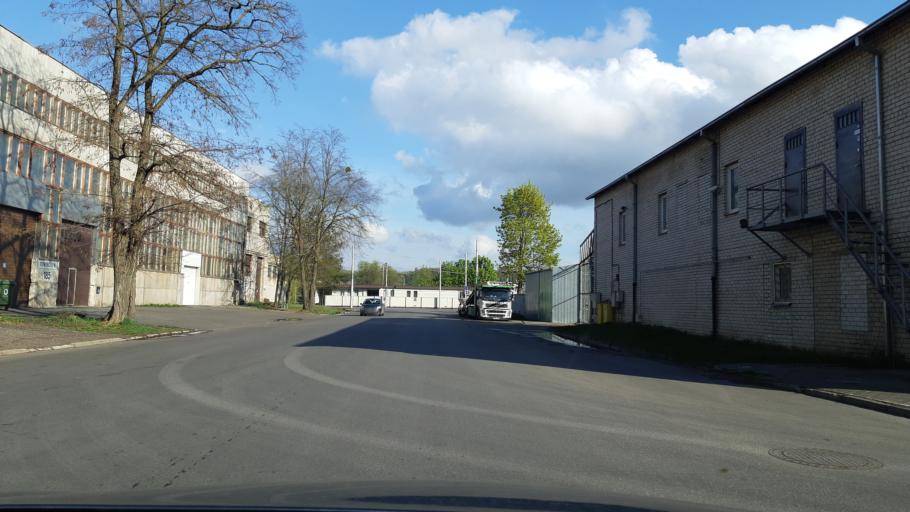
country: LT
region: Kauno apskritis
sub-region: Kaunas
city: Aleksotas
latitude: 54.8629
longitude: 23.9474
